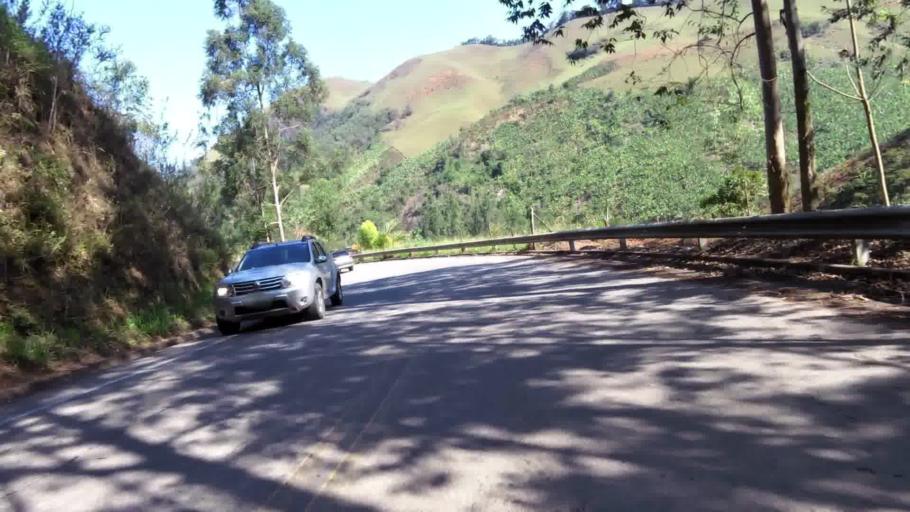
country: BR
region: Espirito Santo
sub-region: Alfredo Chaves
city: Alfredo Chaves
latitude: -20.5973
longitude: -40.7960
